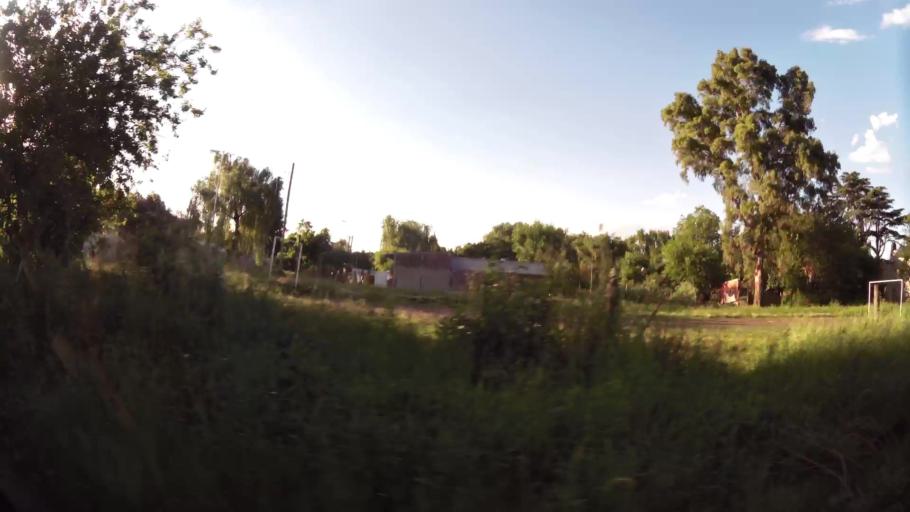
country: AR
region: Buenos Aires
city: Santa Catalina - Dique Lujan
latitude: -34.4699
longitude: -58.7470
